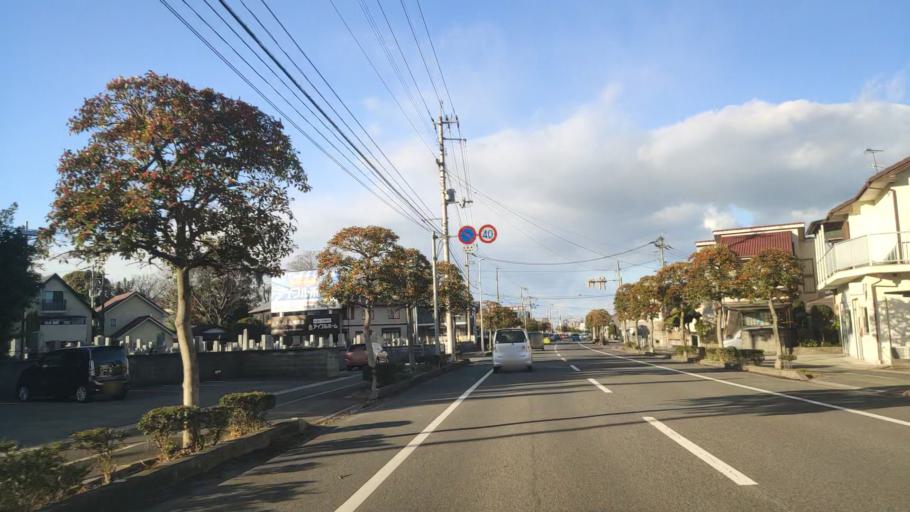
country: JP
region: Ehime
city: Saijo
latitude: 33.9221
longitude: 133.1843
